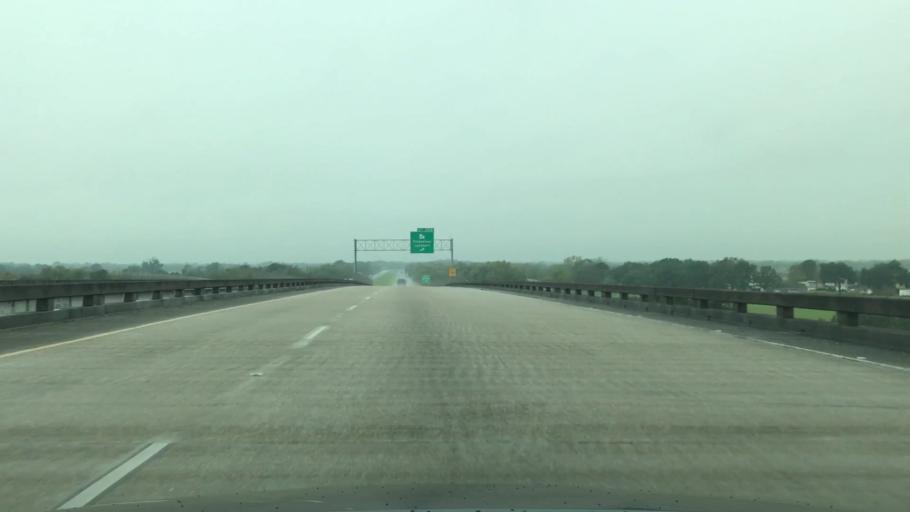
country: US
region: Louisiana
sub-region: Lafourche Parish
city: Raceland
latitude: 29.7082
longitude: -90.5719
